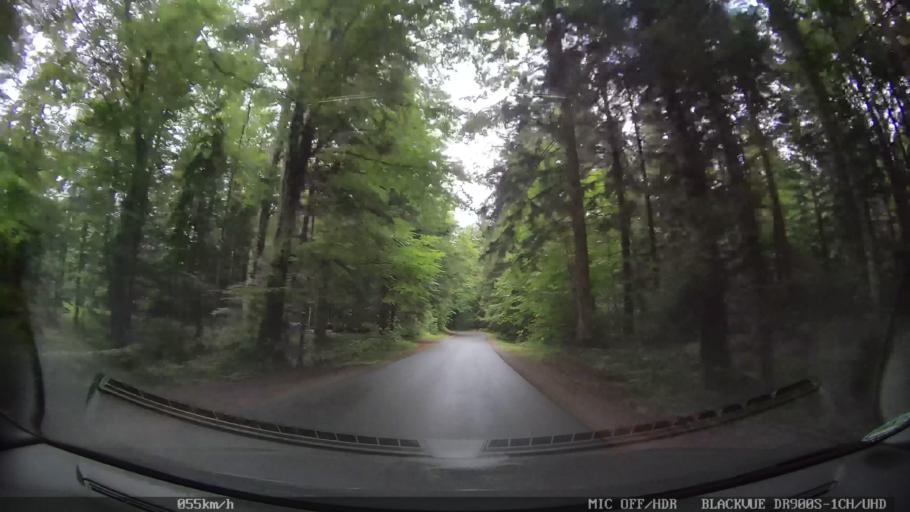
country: HR
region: Licko-Senjska
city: Jezerce
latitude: 44.9327
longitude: 15.5519
